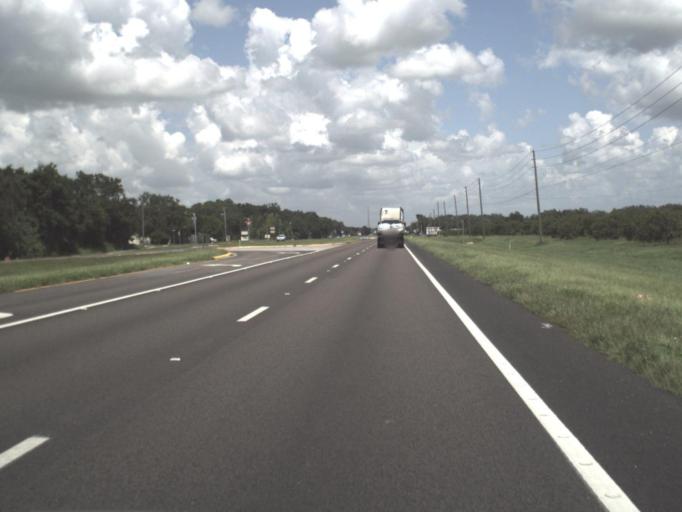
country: US
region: Florida
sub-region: Hardee County
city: Wauchula
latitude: 27.5796
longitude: -81.8183
